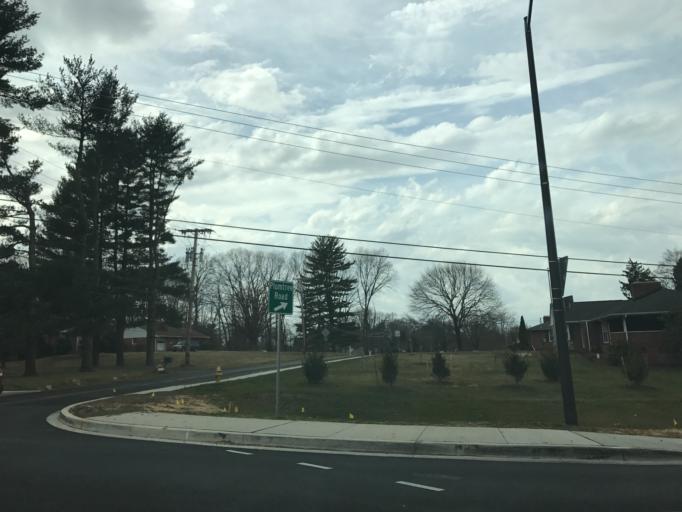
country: US
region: Maryland
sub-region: Harford County
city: Bel Air South
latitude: 39.5007
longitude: -76.3335
